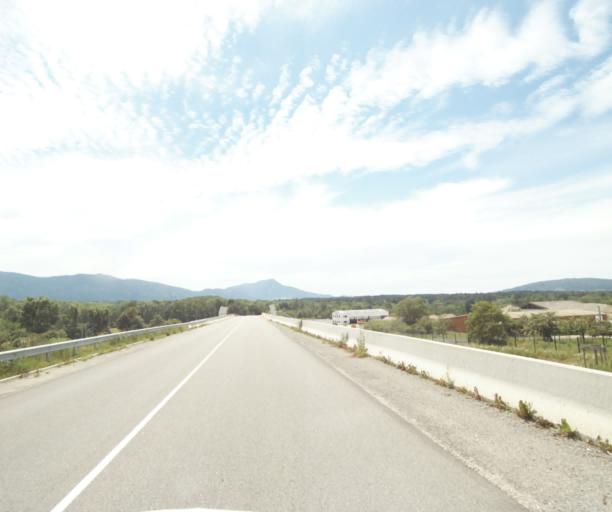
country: FR
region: Rhone-Alpes
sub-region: Departement de la Haute-Savoie
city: Margencel
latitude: 46.3246
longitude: 6.4410
